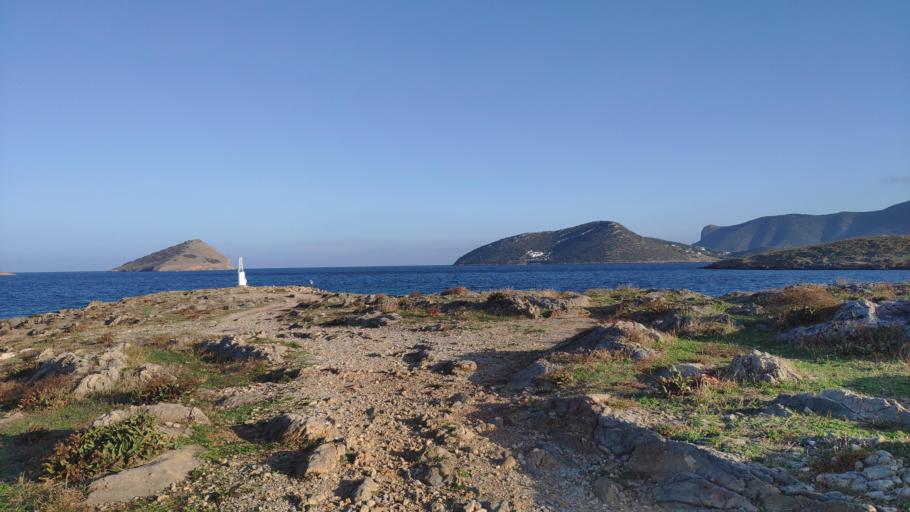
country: GR
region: Attica
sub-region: Nomarchia Anatolikis Attikis
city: Limin Mesoyaias
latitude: 37.8846
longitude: 24.0204
